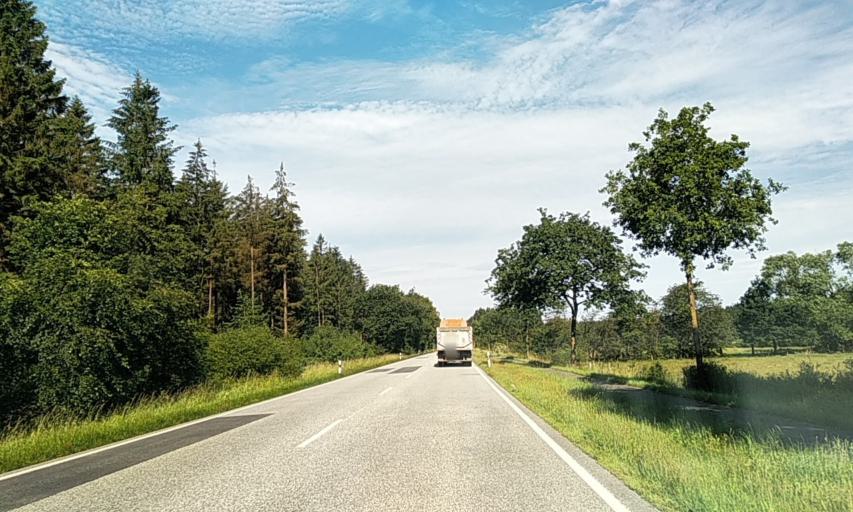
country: DE
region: Schleswig-Holstein
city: Lohe-Fohrden
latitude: 54.3520
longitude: 9.5658
